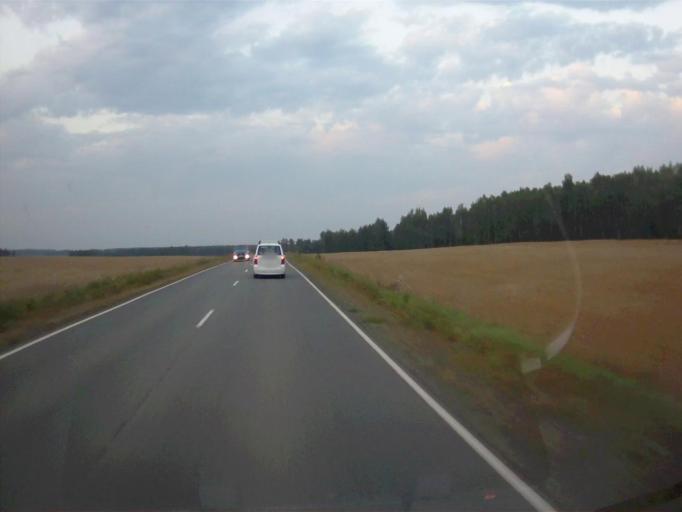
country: RU
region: Chelyabinsk
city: Chebarkul'
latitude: 55.1714
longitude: 60.4516
